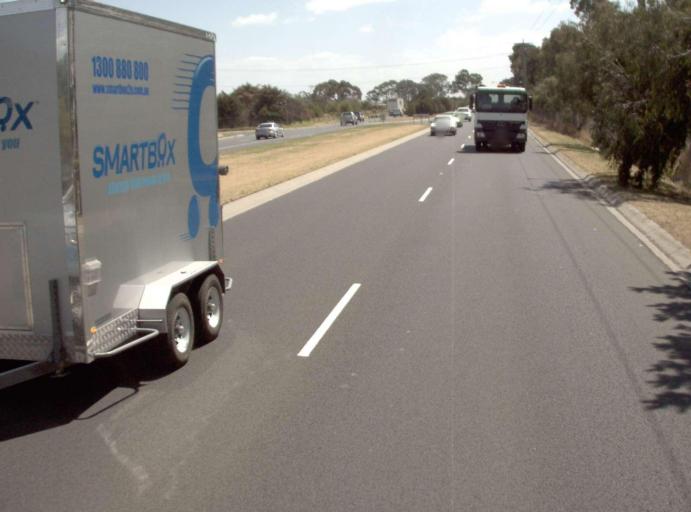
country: AU
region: Victoria
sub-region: Kingston
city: Waterways
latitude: -38.0122
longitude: 145.1537
